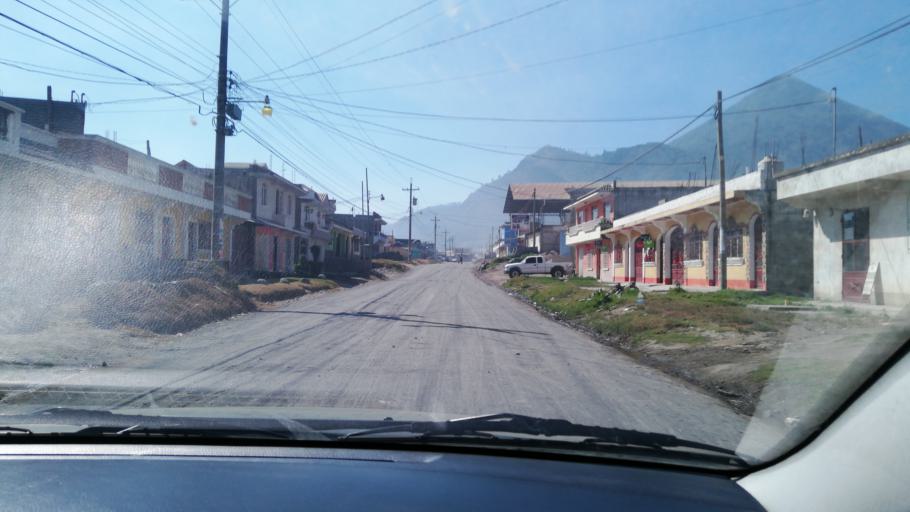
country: GT
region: Quetzaltenango
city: Quetzaltenango
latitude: 14.8003
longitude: -91.5503
